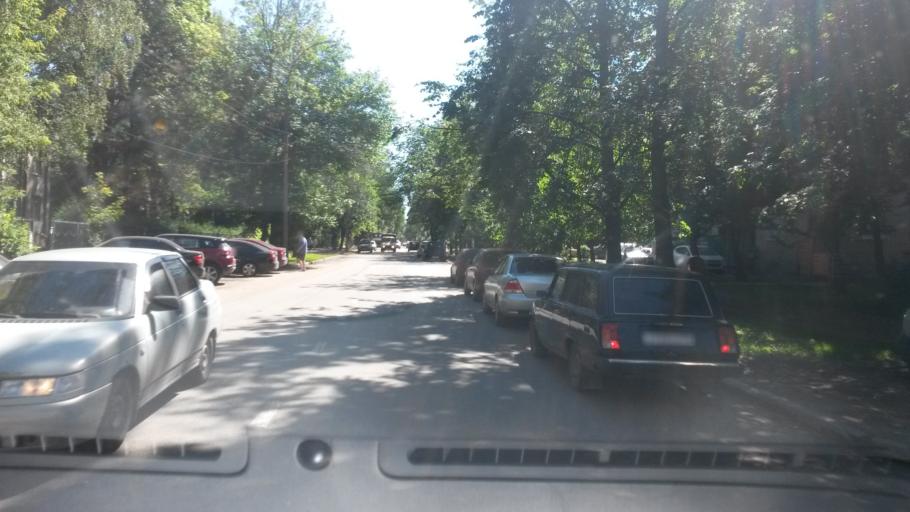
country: RU
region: Jaroslavl
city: Yaroslavl
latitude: 57.6315
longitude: 39.8602
